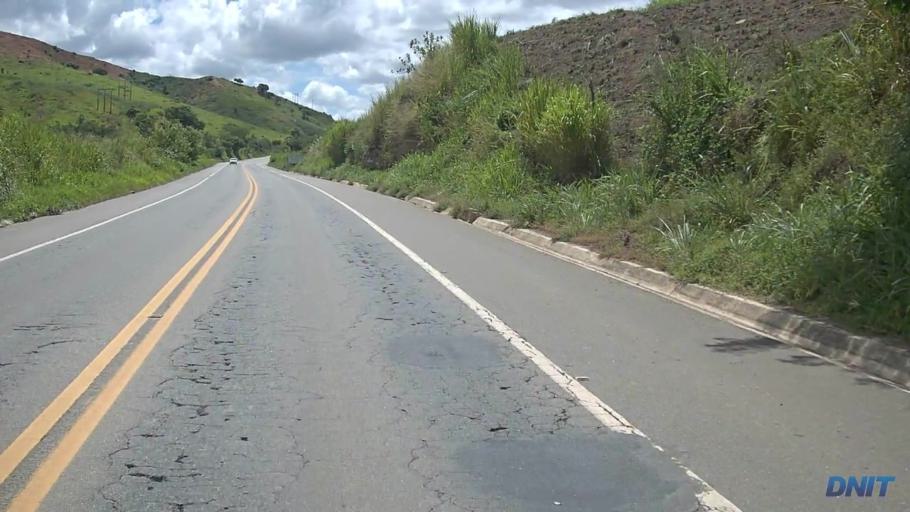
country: BR
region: Minas Gerais
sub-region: Governador Valadares
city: Governador Valadares
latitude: -18.8784
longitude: -41.9935
